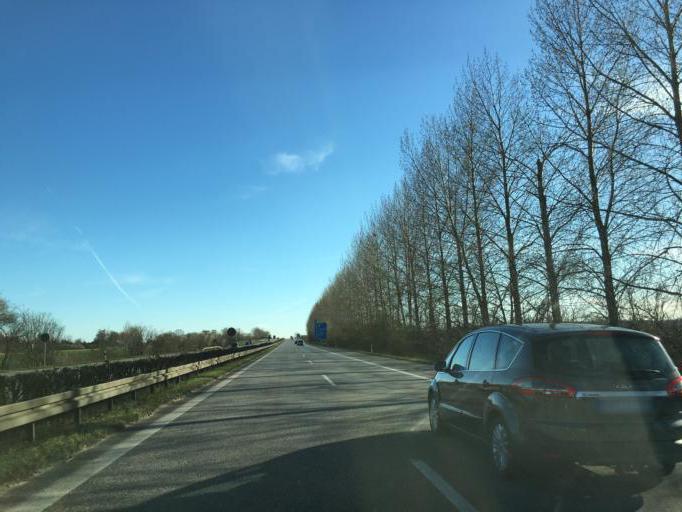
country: DE
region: Mecklenburg-Vorpommern
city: Roggentin
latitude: 54.0876
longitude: 12.1989
